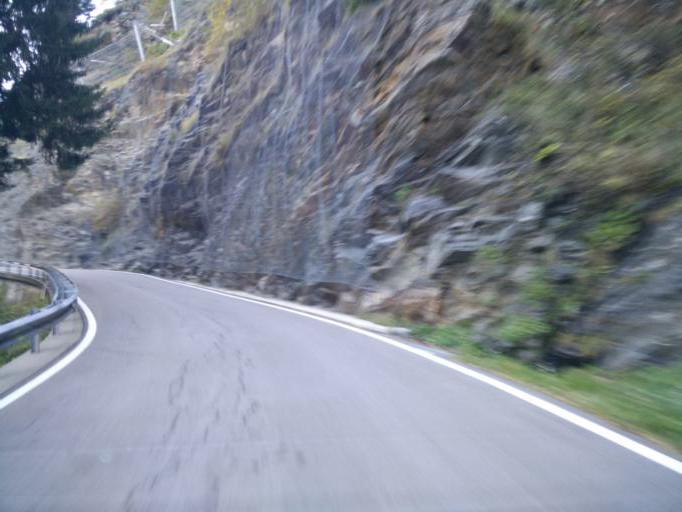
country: IT
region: Trentino-Alto Adige
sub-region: Bolzano
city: Moso in Passiria
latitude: 46.8376
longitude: 11.1701
